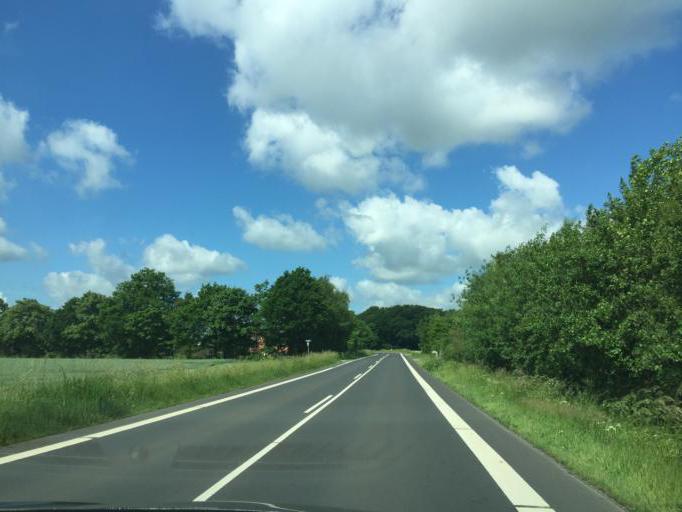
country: DK
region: South Denmark
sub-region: Fredericia Kommune
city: Snoghoj
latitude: 55.5355
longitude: 9.6821
